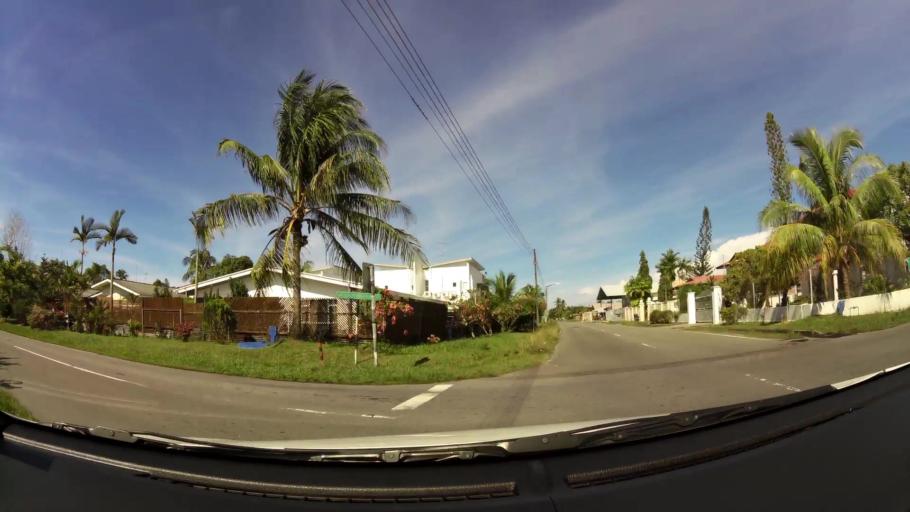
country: BN
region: Belait
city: Kuala Belait
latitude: 4.5866
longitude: 114.2108
